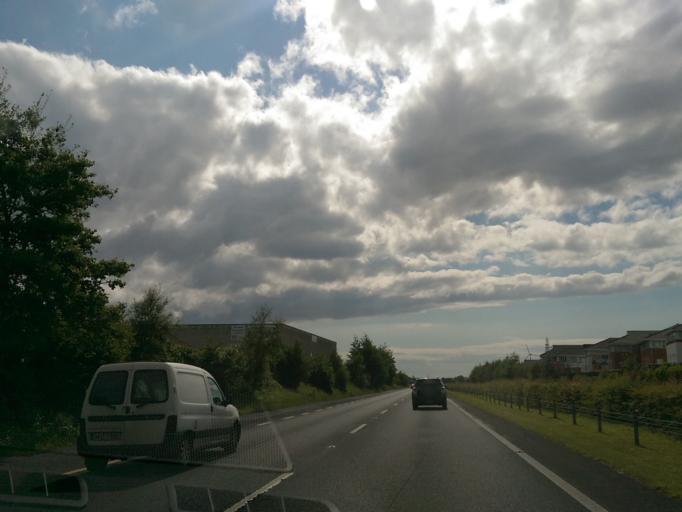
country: IE
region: Connaught
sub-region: County Galway
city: Gaillimh
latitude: 53.2911
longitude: -8.9995
